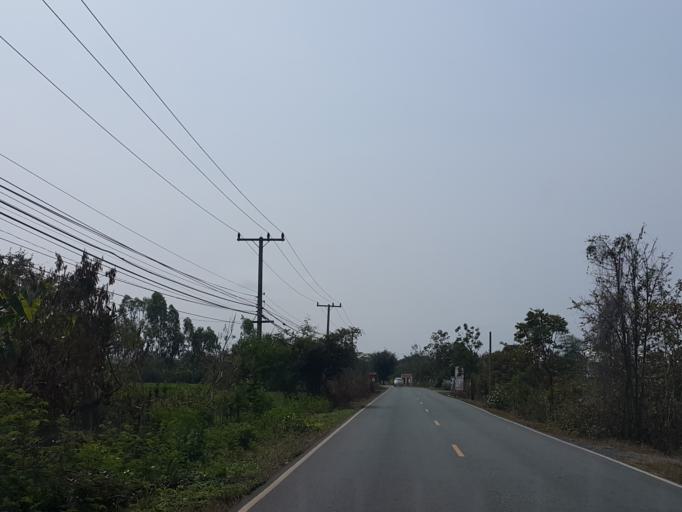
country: TH
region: Chiang Mai
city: San Kamphaeng
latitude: 18.6913
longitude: 99.1027
